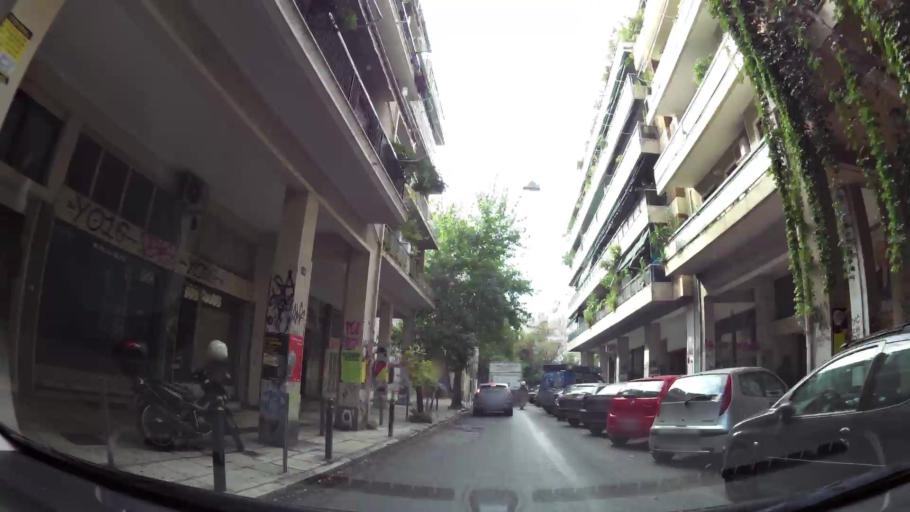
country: GR
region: Attica
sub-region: Nomarchia Athinas
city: Kipseli
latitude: 37.9890
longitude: 23.7352
